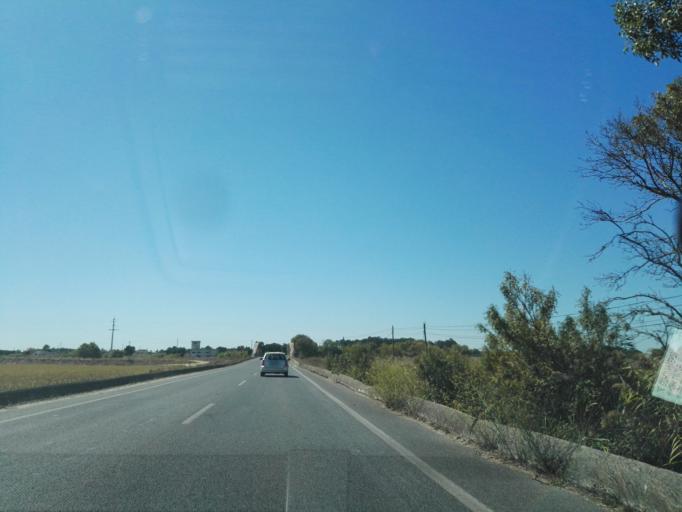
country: PT
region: Santarem
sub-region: Benavente
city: Samora Correia
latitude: 38.9391
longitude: -8.8431
